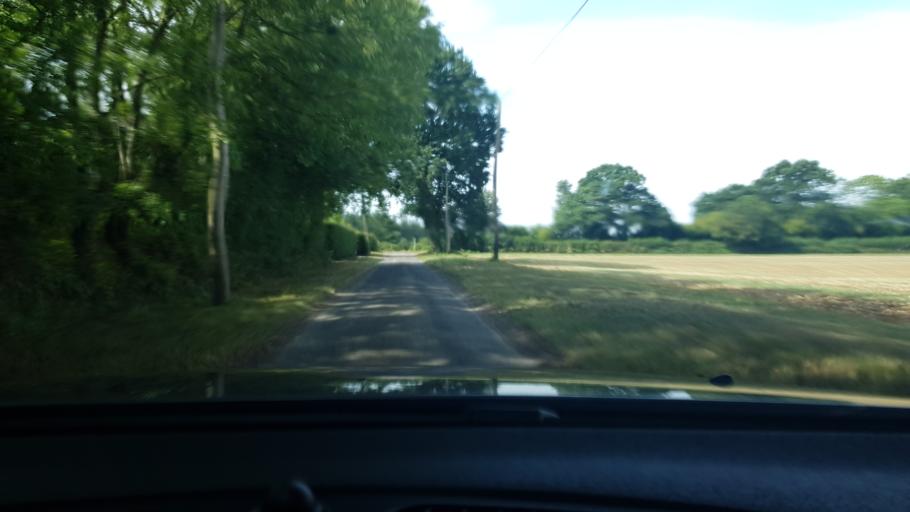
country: GB
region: England
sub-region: Wiltshire
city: Shalbourne
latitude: 51.3665
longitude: -1.5711
